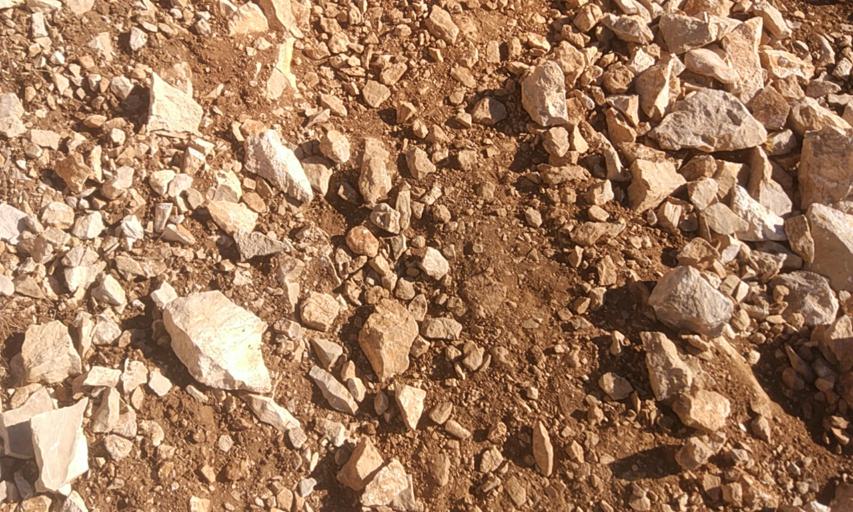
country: TR
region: Antalya
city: Altinyaka
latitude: 36.5387
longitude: 30.4392
